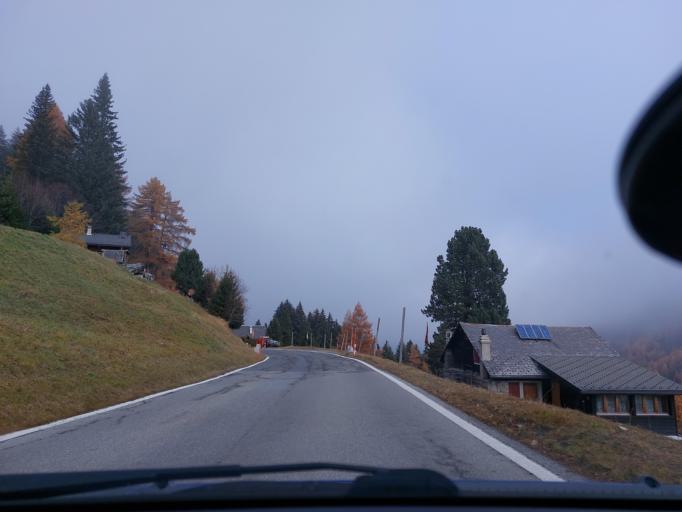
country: CH
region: Valais
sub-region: Conthey District
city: Basse-Nendaz
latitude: 46.1519
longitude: 7.3153
